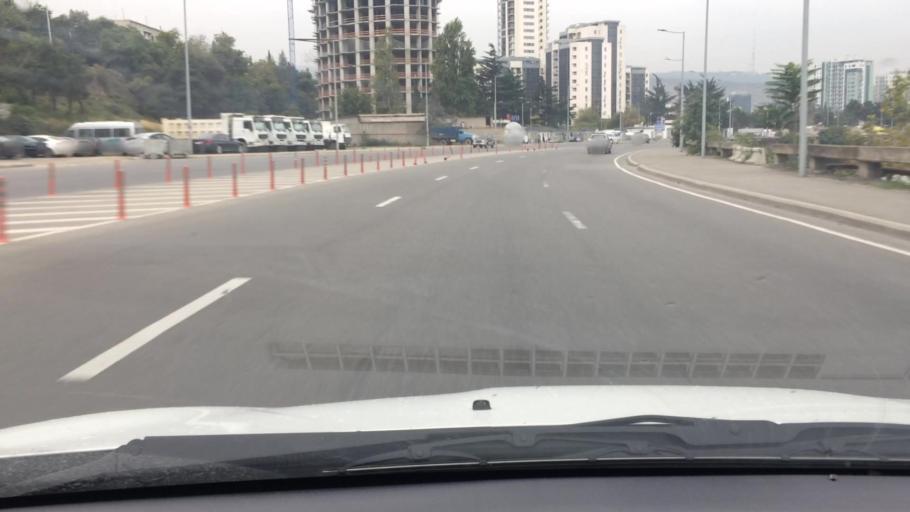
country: GE
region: T'bilisi
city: Tbilisi
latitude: 41.6718
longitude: 44.8396
